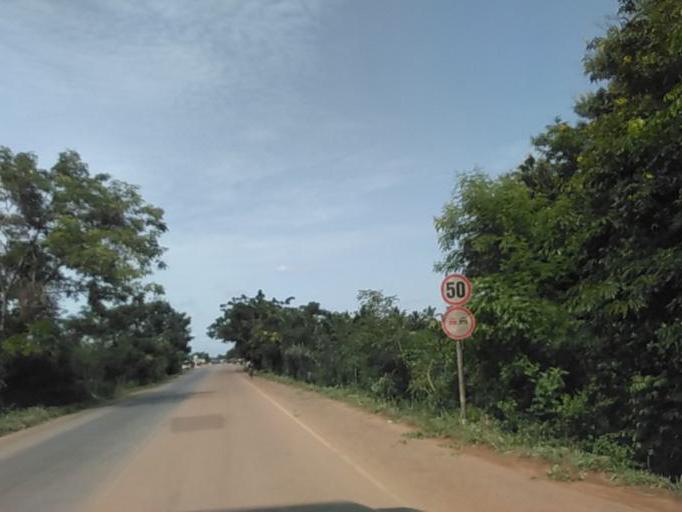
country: GH
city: Akropong
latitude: 6.1667
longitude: 0.0657
